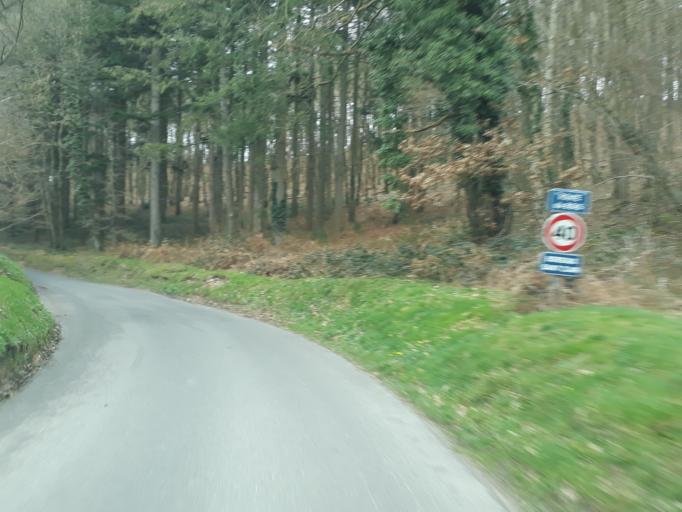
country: FR
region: Haute-Normandie
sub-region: Departement de la Seine-Maritime
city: Les Loges
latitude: 49.6801
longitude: 0.2569
